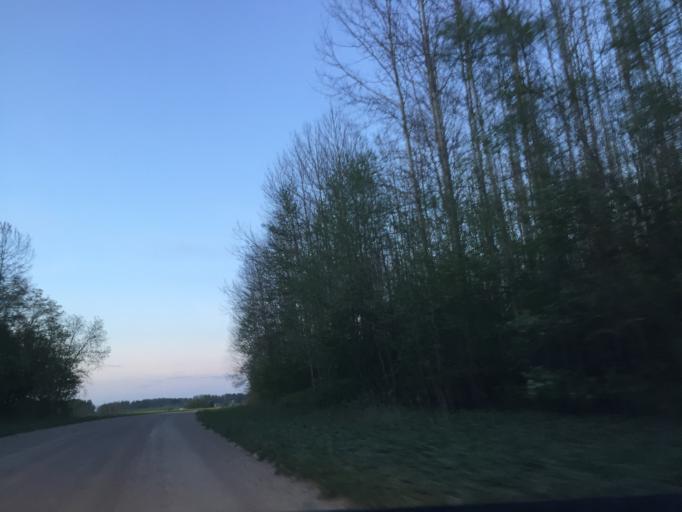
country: LV
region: Bauskas Rajons
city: Bauska
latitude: 56.4804
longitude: 24.1048
